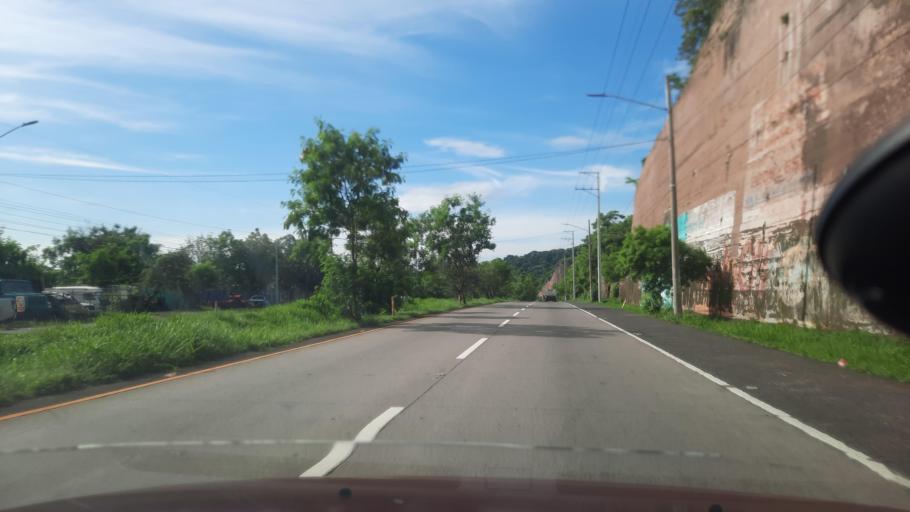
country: SV
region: La Paz
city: Olocuilta
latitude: 13.5206
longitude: -89.1023
